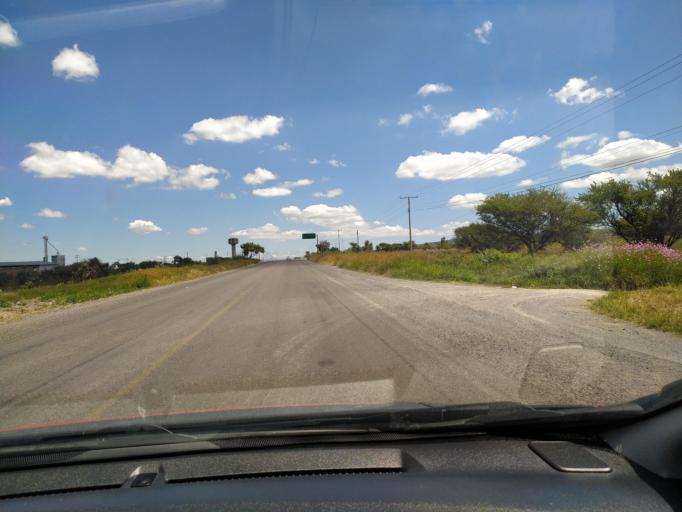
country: MX
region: Jalisco
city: San Diego de Alejandria
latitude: 21.0049
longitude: -101.9790
